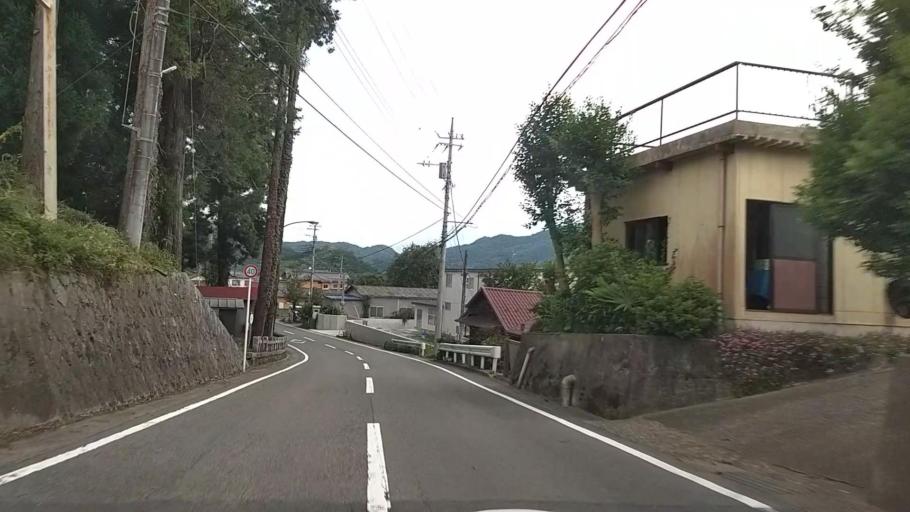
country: JP
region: Yamanashi
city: Uenohara
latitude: 35.6192
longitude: 139.1255
